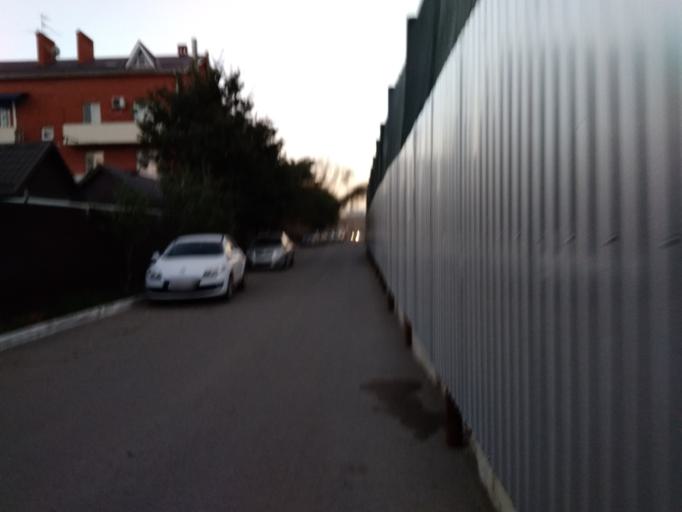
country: RU
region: Krasnodarskiy
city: Krasnodar
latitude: 45.0786
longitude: 39.0040
